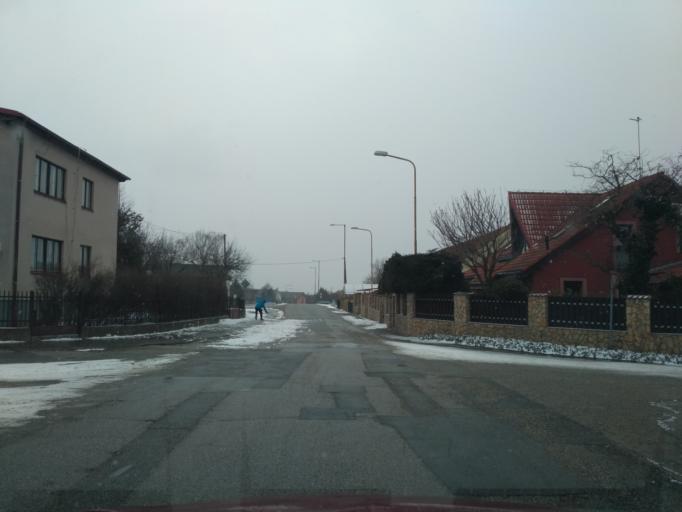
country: SK
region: Kosicky
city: Kosice
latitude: 48.7141
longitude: 21.2221
